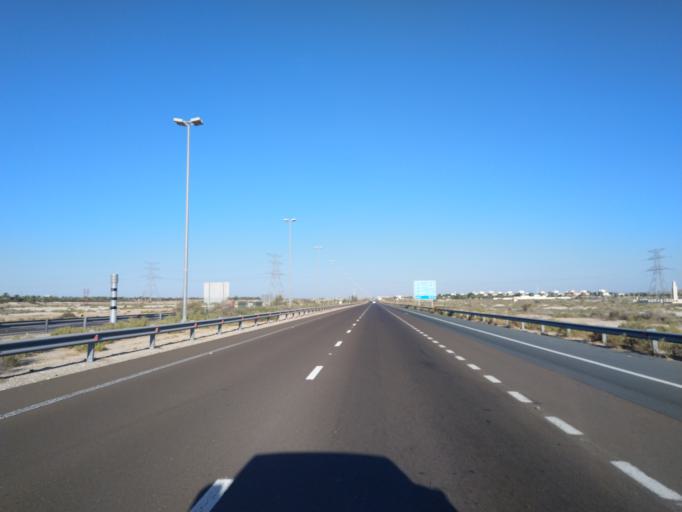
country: OM
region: Al Buraimi
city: Al Buraymi
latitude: 24.5196
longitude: 55.5176
